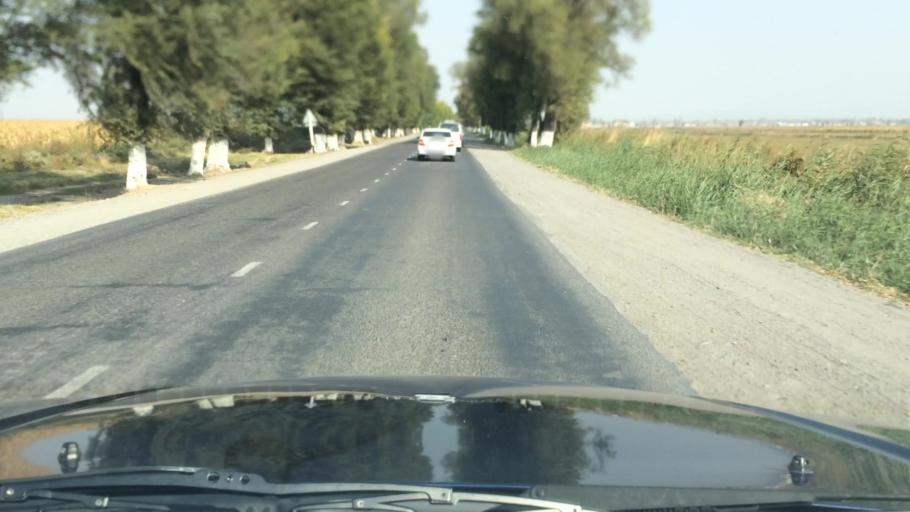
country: KG
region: Chuy
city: Lebedinovka
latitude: 42.9016
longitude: 74.6854
